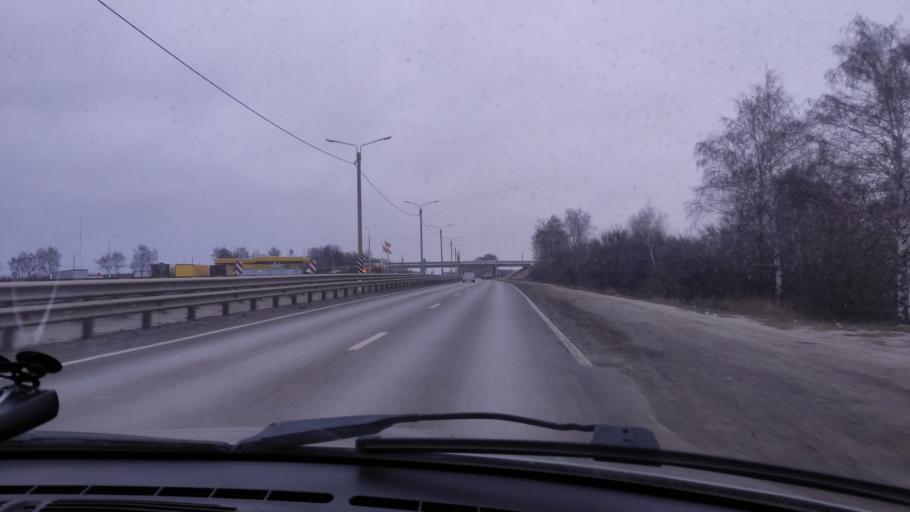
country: RU
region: Tambov
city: Komsomolets
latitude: 52.7330
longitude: 41.3005
